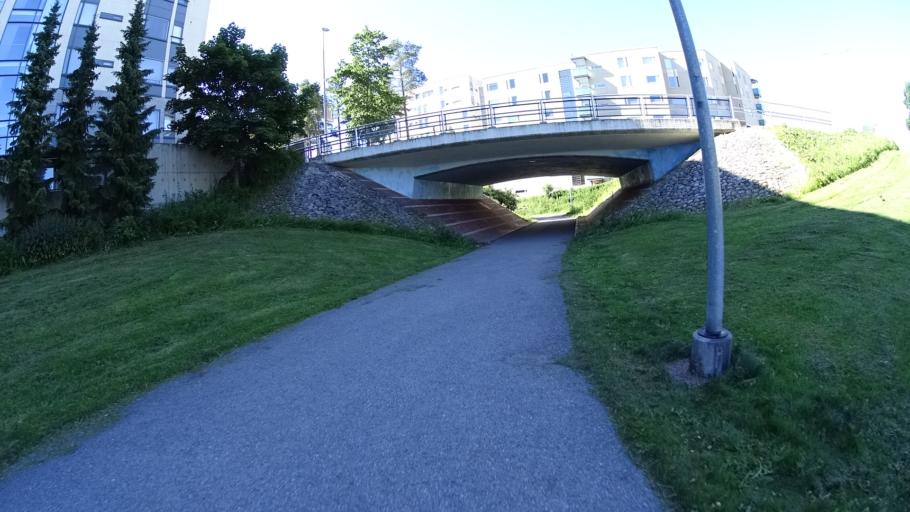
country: FI
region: Uusimaa
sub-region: Helsinki
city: Koukkuniemi
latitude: 60.1624
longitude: 24.7436
